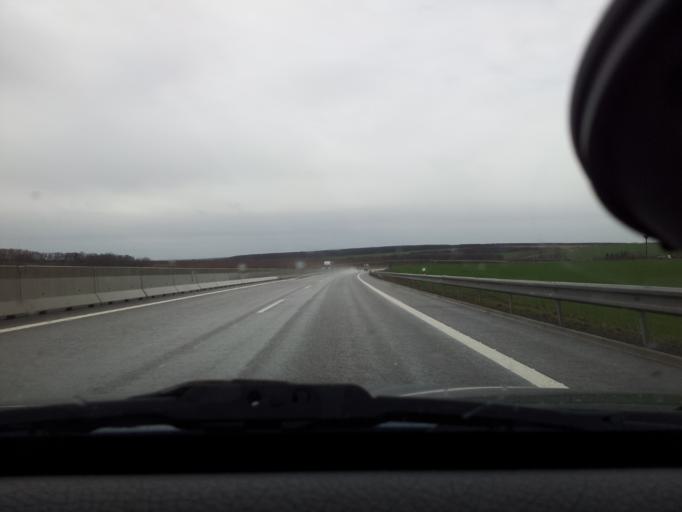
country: SK
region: Nitriansky
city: Zlate Moravce
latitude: 48.3461
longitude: 18.4323
